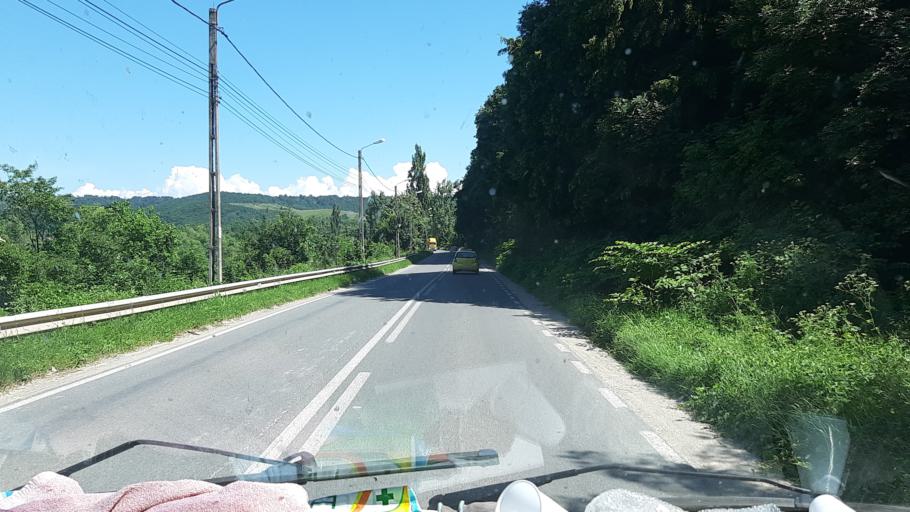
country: RO
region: Caras-Severin
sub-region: Oras Bocsa
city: Bocsa
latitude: 45.3794
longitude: 21.7437
